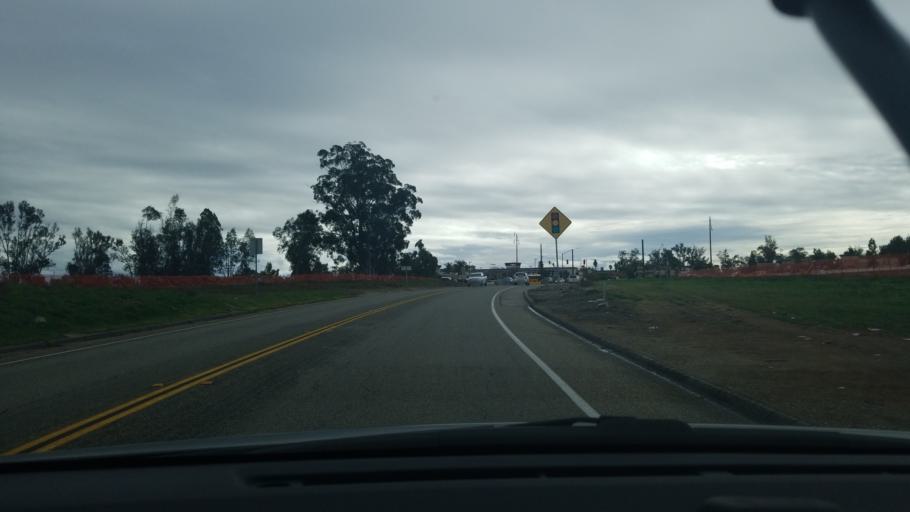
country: US
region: California
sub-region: Riverside County
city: Sun City
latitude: 33.6435
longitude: -117.1687
